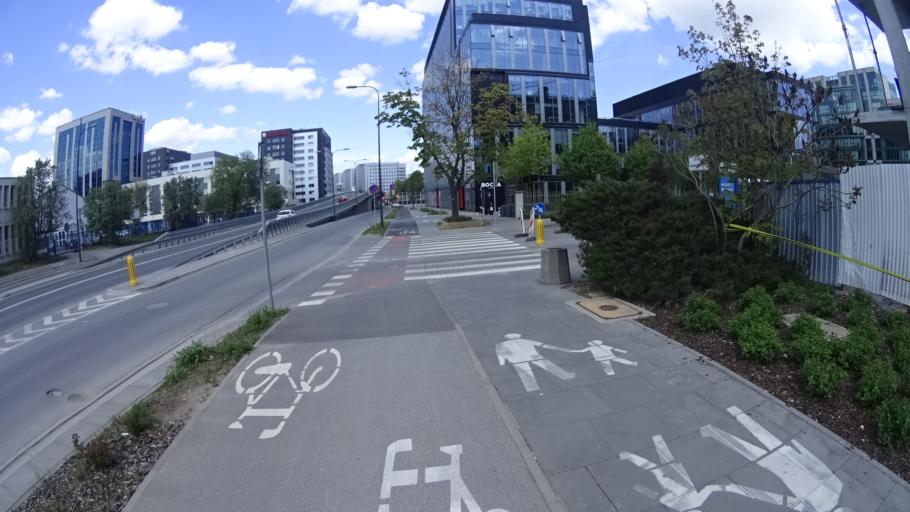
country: PL
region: Masovian Voivodeship
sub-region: Warszawa
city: Mokotow
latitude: 52.1777
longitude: 20.9964
